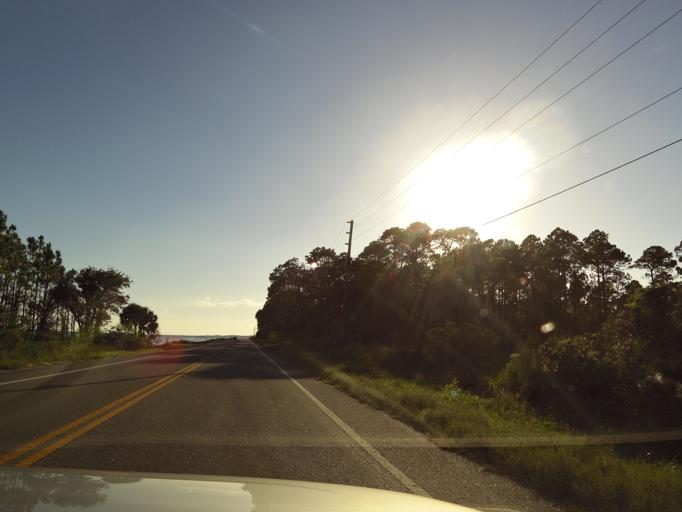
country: US
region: Florida
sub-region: Franklin County
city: Eastpoint
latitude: 29.7612
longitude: -84.8186
